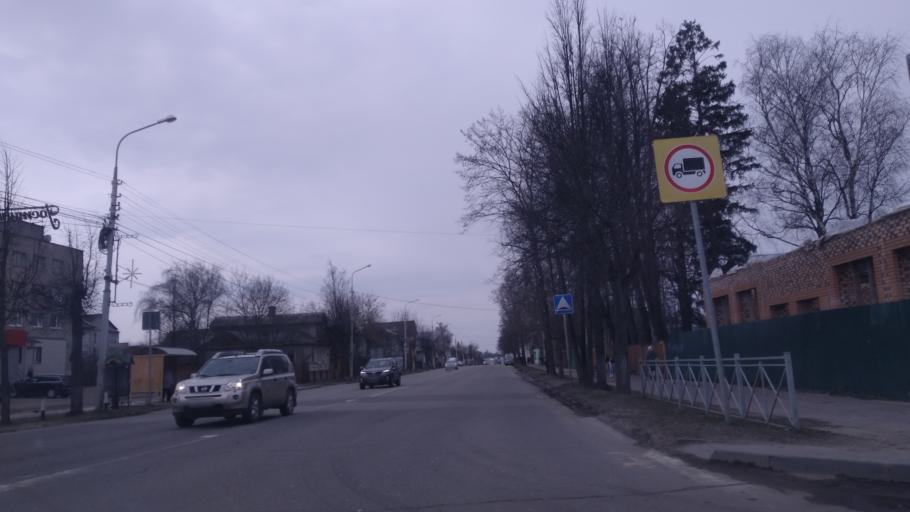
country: RU
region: Jaroslavl
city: Uglich
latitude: 57.5323
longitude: 38.3313
